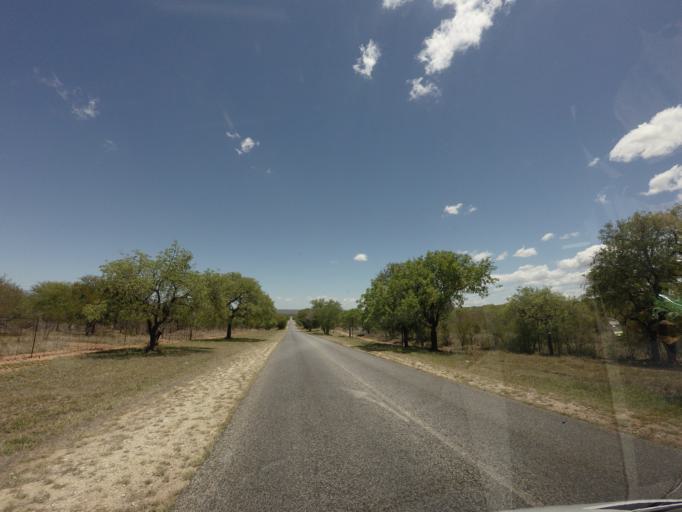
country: ZA
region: Limpopo
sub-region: Mopani District Municipality
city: Hoedspruit
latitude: -24.3805
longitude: 30.7387
